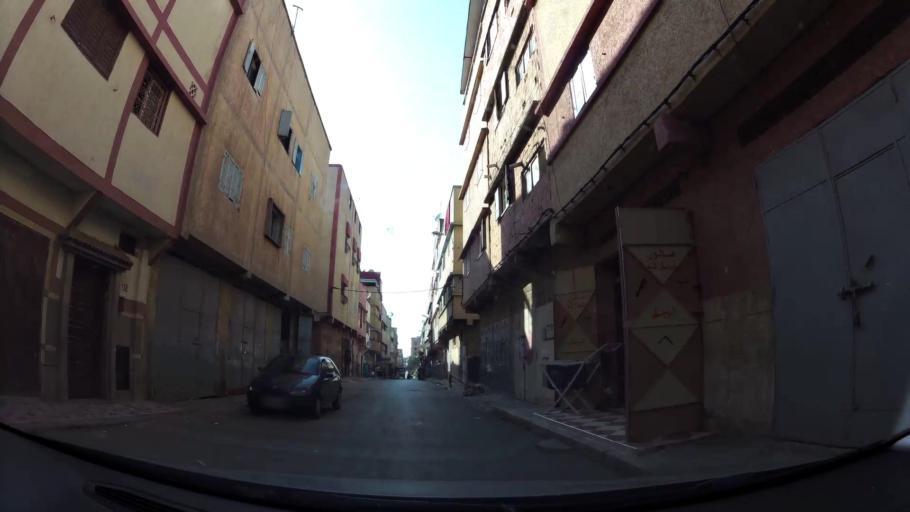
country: MA
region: Rabat-Sale-Zemmour-Zaer
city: Sale
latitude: 34.0526
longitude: -6.7746
